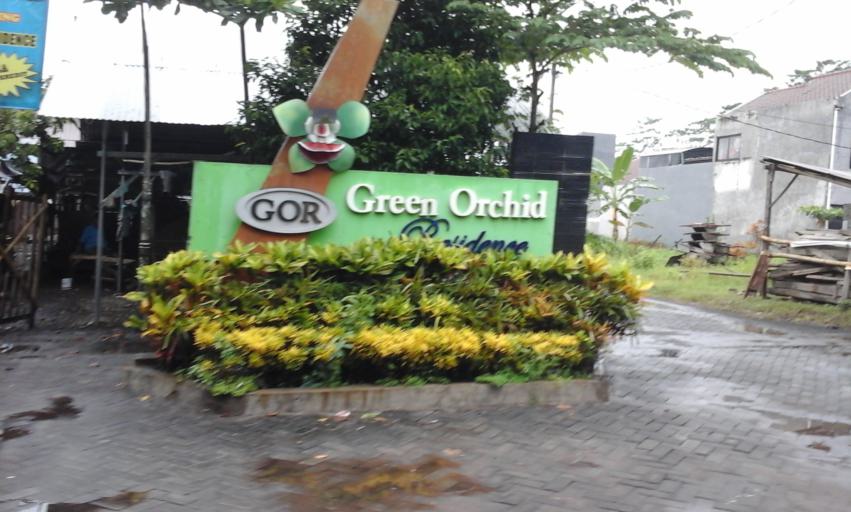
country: ID
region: East Java
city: Lumajang
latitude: -8.1279
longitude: 113.2191
